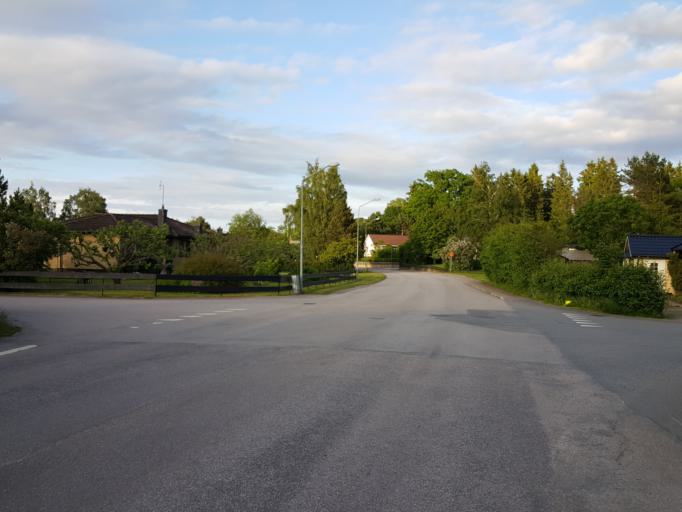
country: SE
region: Uppsala
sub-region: Osthammars Kommun
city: Gimo
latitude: 60.1686
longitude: 18.1810
